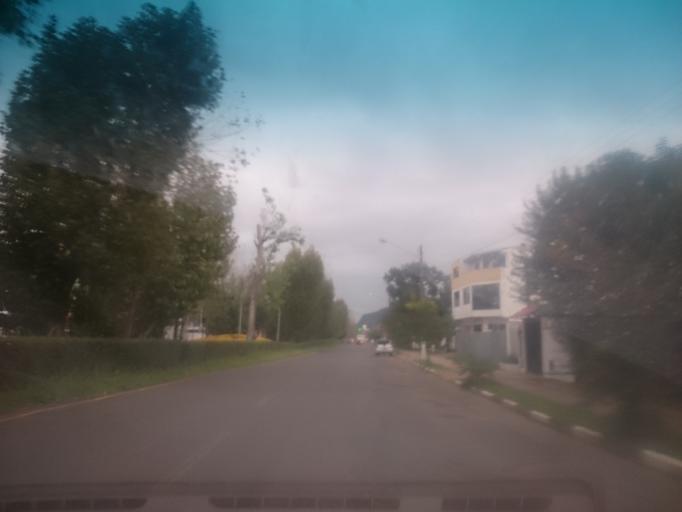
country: BR
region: Santa Catarina
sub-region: Lages
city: Lages
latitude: -27.8133
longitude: -50.3174
